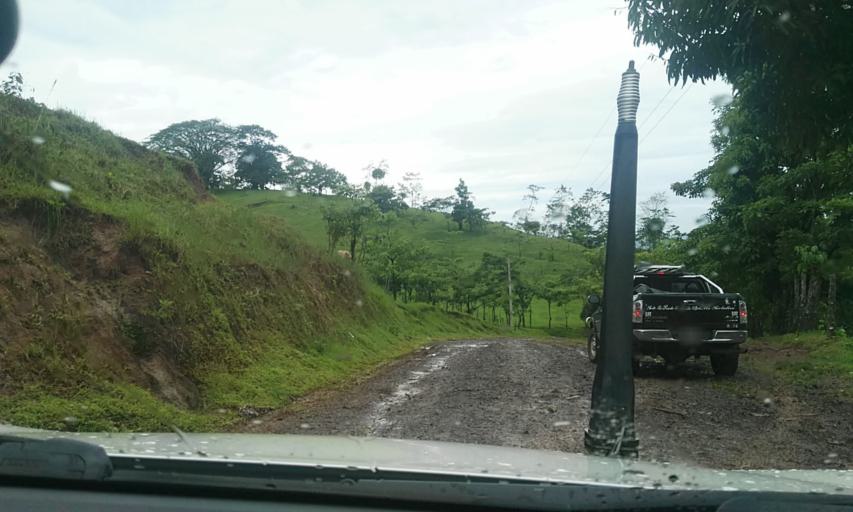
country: NI
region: Matagalpa
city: Rio Blanco
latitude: 12.9979
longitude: -85.1958
